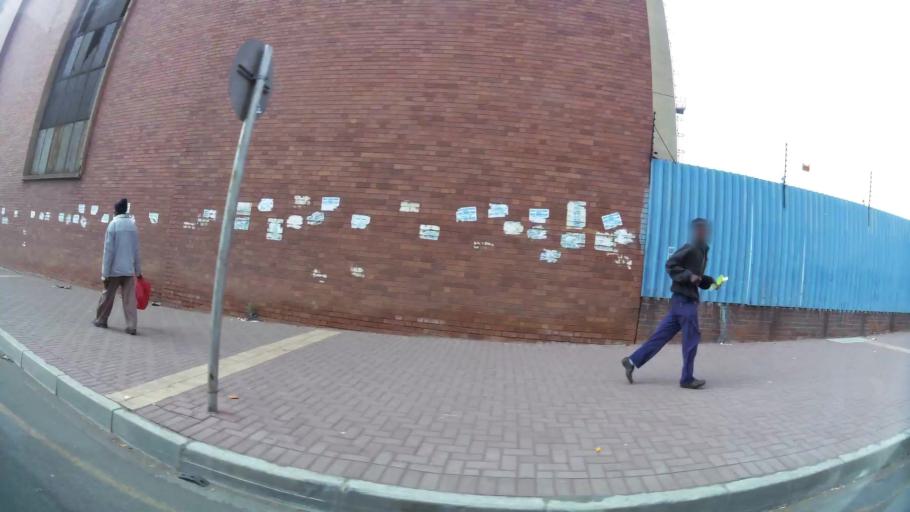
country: ZA
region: Orange Free State
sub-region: Mangaung Metropolitan Municipality
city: Bloemfontein
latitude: -29.1240
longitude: 26.2245
